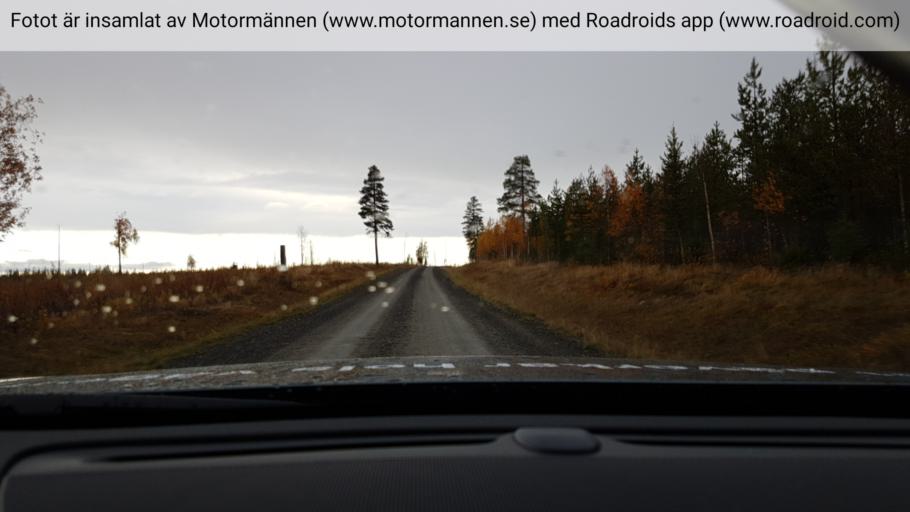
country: SE
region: Norrbotten
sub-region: Pajala Kommun
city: Pajala
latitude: 67.0773
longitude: 22.7872
